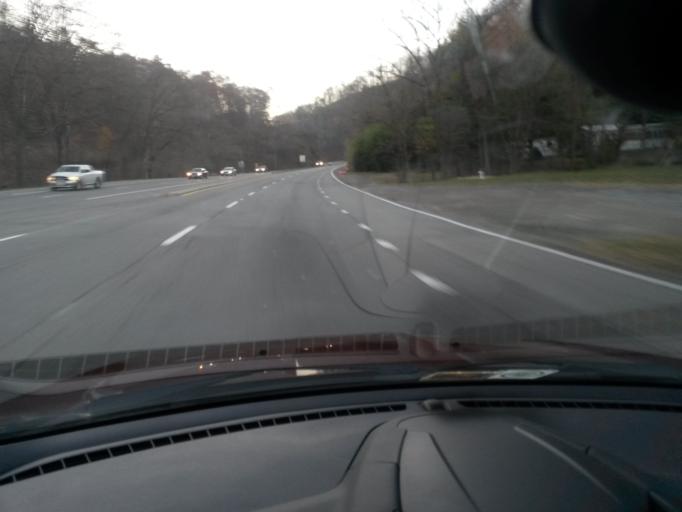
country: US
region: Virginia
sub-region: Roanoke County
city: Narrows
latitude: 37.1982
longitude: -79.9432
